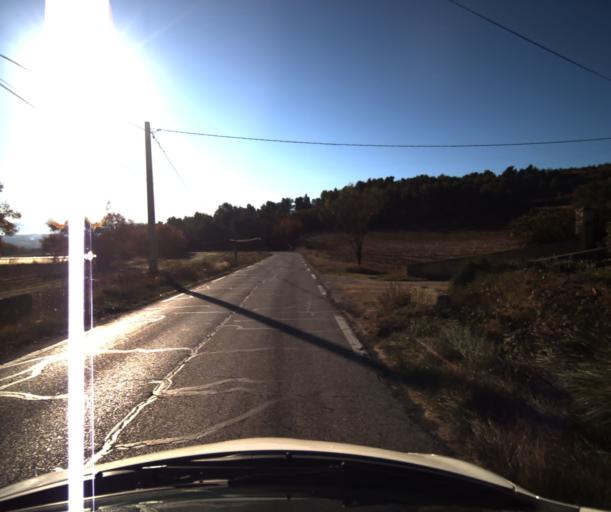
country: FR
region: Provence-Alpes-Cote d'Azur
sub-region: Departement du Vaucluse
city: Pertuis
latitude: 43.7199
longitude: 5.5042
